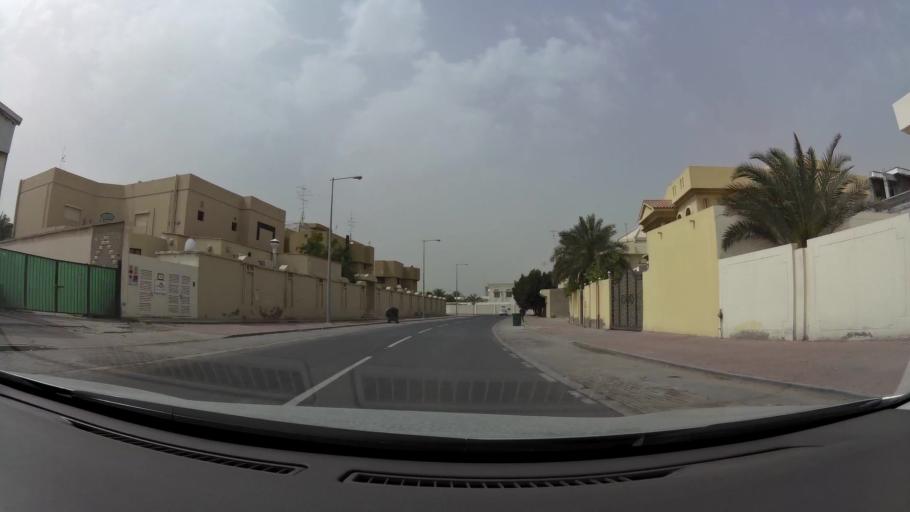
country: QA
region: Baladiyat ad Dawhah
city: Doha
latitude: 25.2623
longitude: 51.5515
